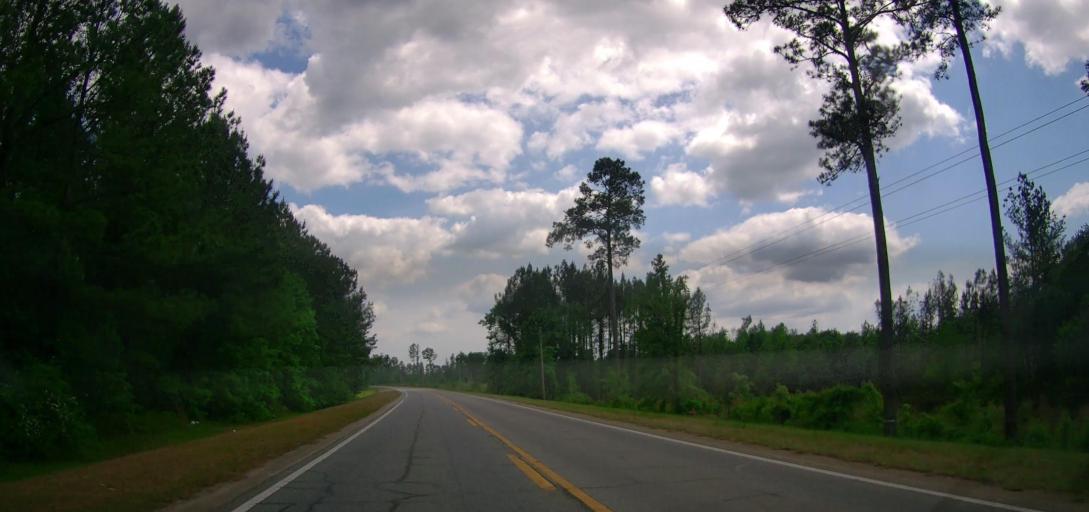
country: US
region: Georgia
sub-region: Laurens County
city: East Dublin
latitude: 32.4927
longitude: -82.8281
